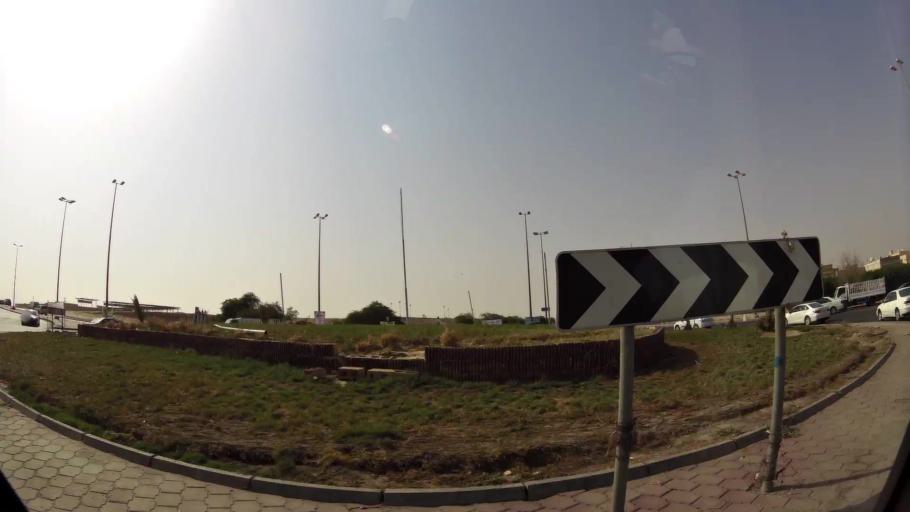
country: KW
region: Muhafazat al Jahra'
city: Al Jahra'
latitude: 29.3194
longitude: 47.6593
